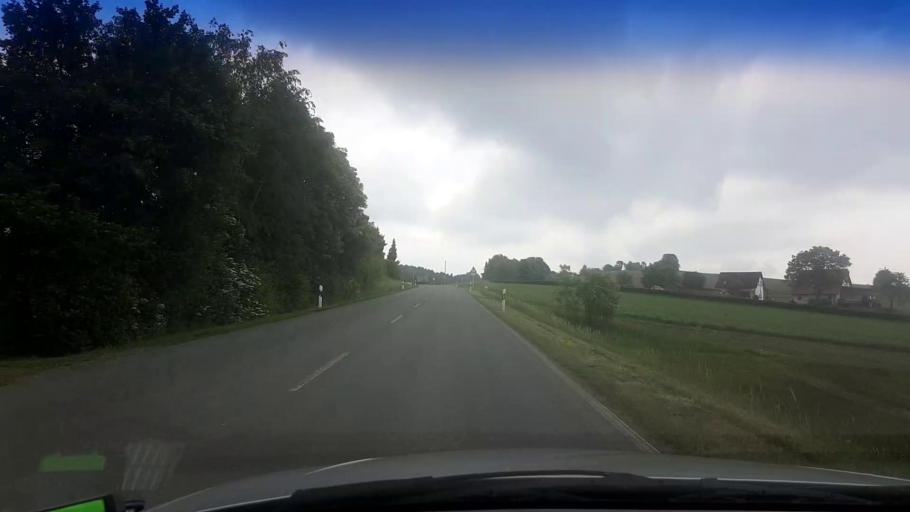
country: DE
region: Bavaria
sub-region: Upper Franconia
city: Reuth
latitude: 49.9924
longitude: 11.6830
